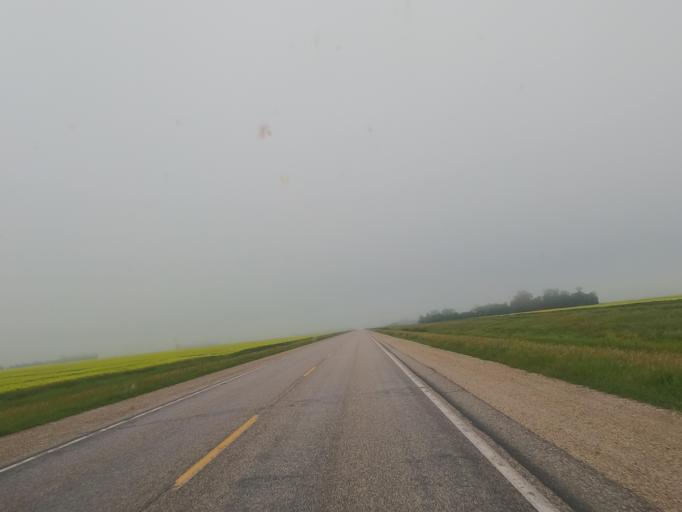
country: CA
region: Manitoba
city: Carman
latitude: 49.7194
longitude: -97.8933
